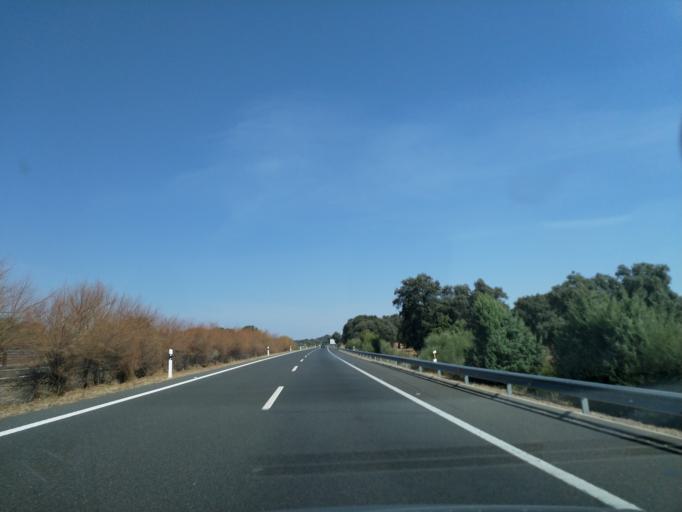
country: ES
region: Extremadura
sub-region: Provincia de Caceres
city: Aldea del Cano
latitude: 39.2986
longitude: -6.3302
